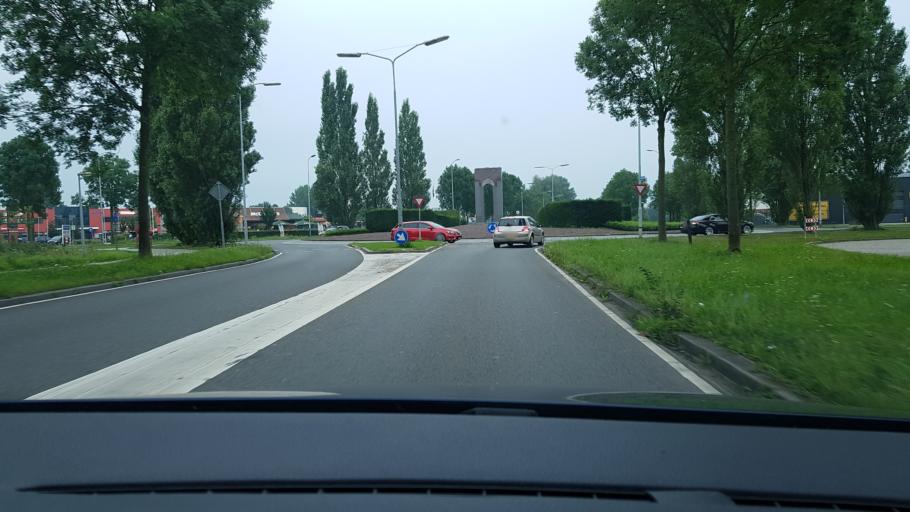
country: NL
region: Gelderland
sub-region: Gemeente Beuningen
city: Beuningen
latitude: 51.8572
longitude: 5.7508
